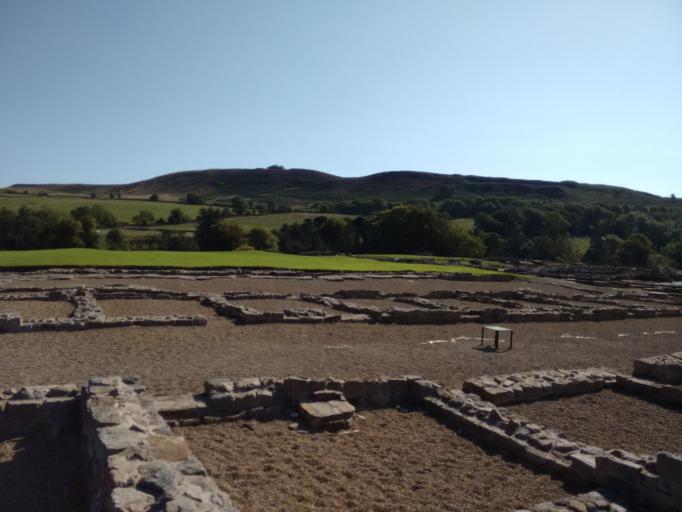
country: GB
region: England
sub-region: Northumberland
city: Bardon Mill
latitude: 54.9916
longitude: -2.3610
